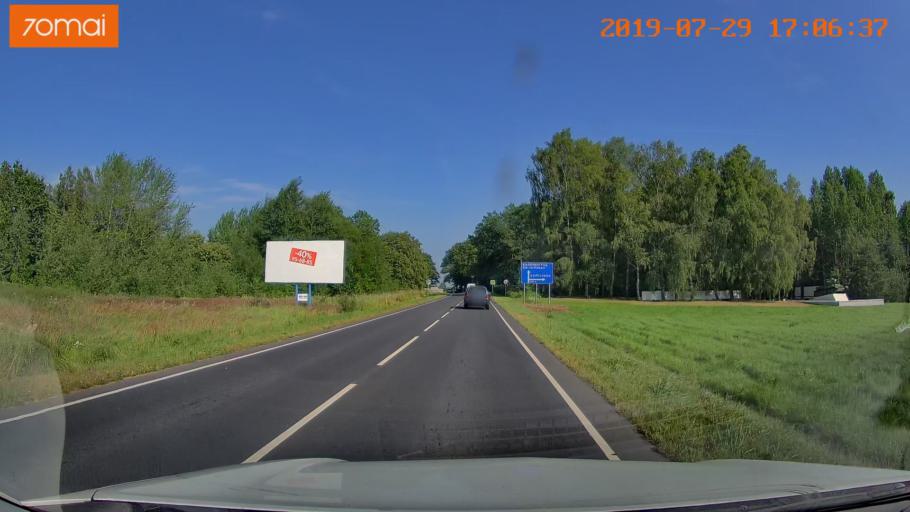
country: RU
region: Kaliningrad
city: Vzmorye
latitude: 54.8195
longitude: 20.3105
